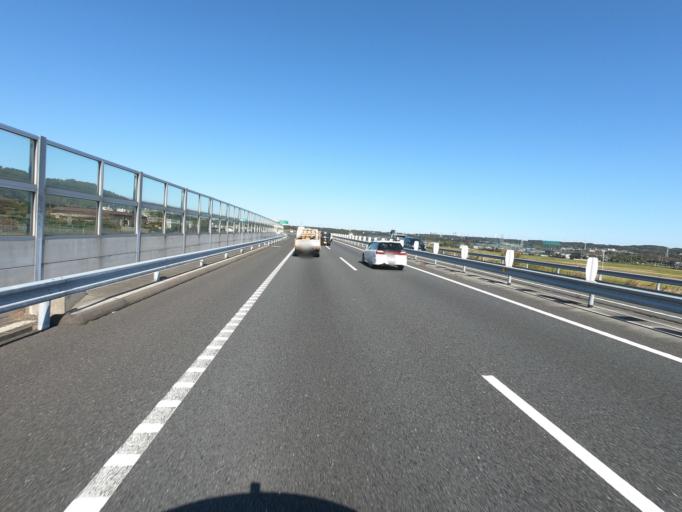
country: JP
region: Kanagawa
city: Zama
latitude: 35.5040
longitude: 139.3656
